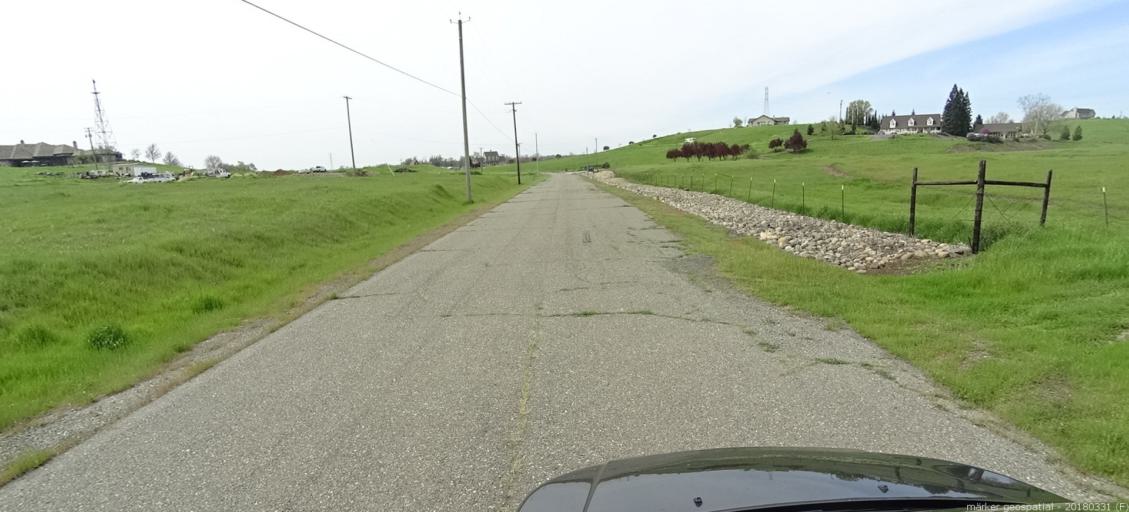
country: US
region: California
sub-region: Sacramento County
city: Rancho Murieta
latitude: 38.4927
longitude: -121.1381
